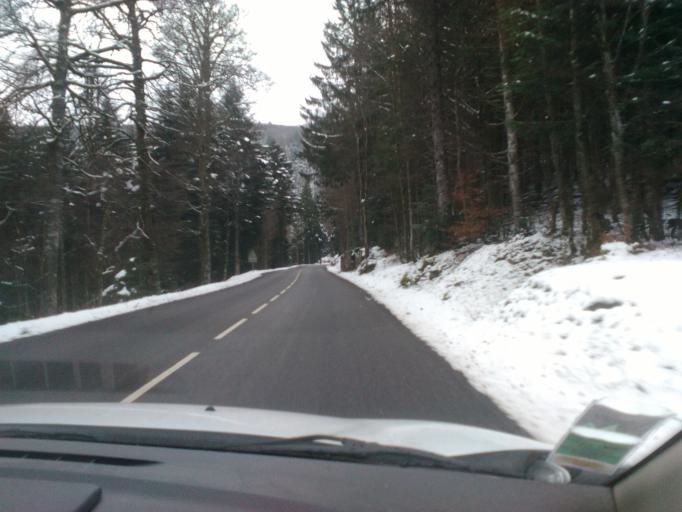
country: FR
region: Lorraine
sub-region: Departement des Vosges
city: Xonrupt-Longemer
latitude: 48.0475
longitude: 6.9948
